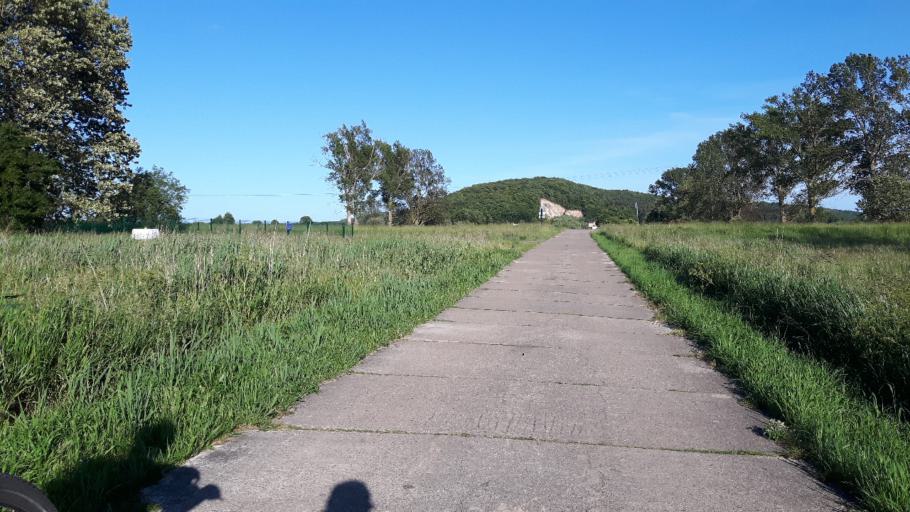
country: PL
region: Pomeranian Voivodeship
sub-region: Powiat wejherowski
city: Rumia
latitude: 54.6070
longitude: 18.4110
